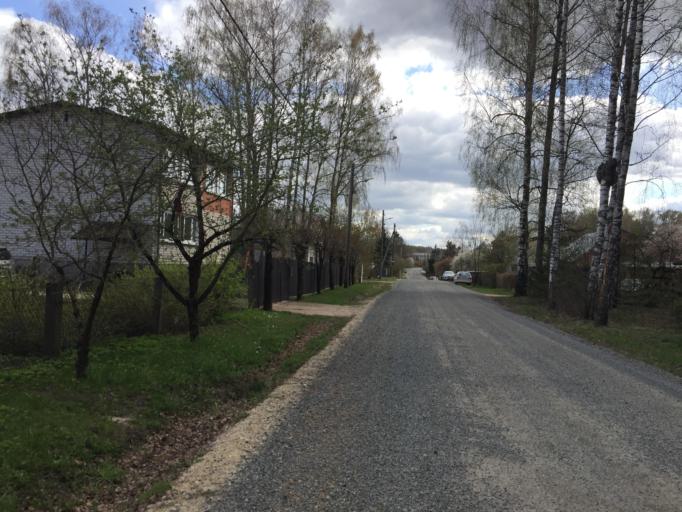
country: LV
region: Baldone
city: Baldone
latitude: 56.7485
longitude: 24.3884
